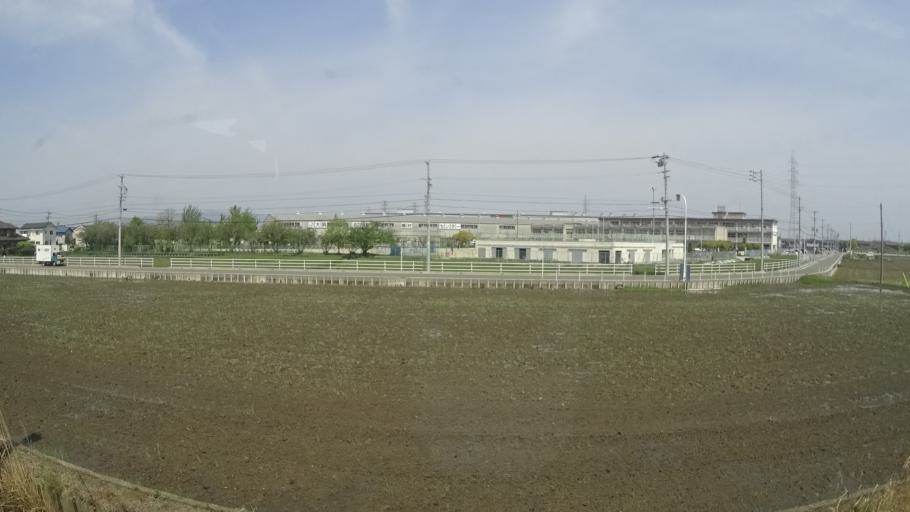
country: JP
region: Aichi
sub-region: Aisai-shi
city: Aisai
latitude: 35.1240
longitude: 136.7479
